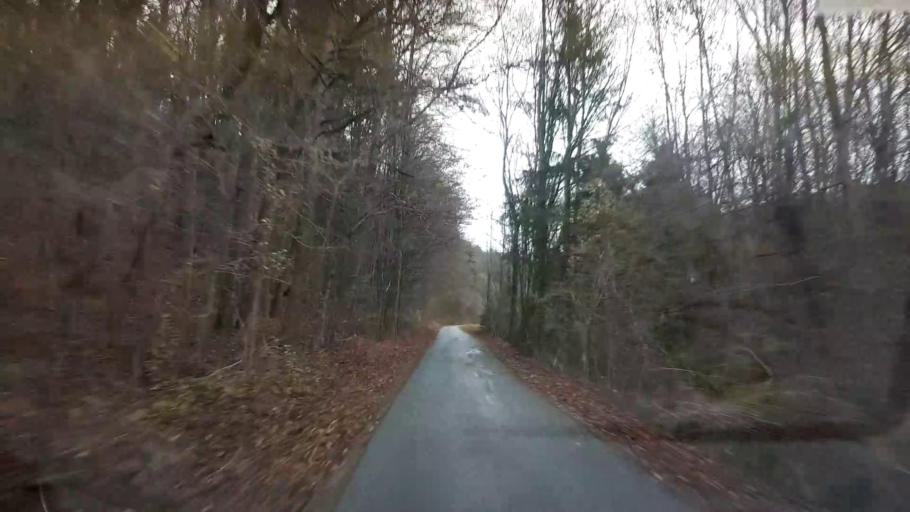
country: DE
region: Bavaria
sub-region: Upper Franconia
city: Wattendorf
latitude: 50.0004
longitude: 11.0926
